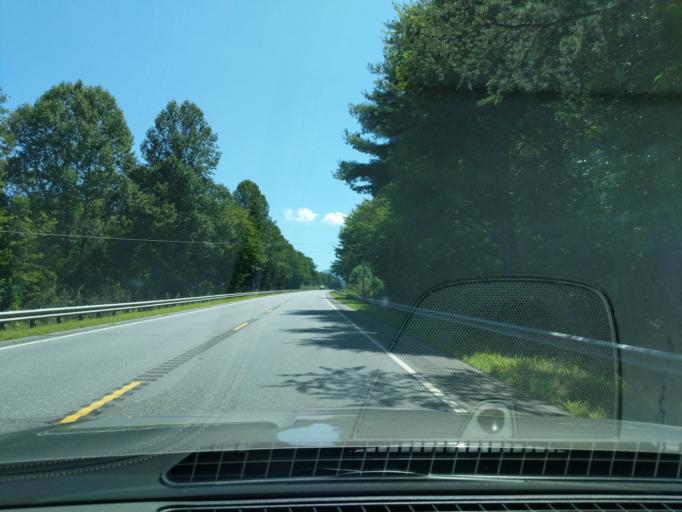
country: US
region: Georgia
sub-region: Towns County
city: Hiawassee
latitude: 35.0314
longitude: -83.7293
